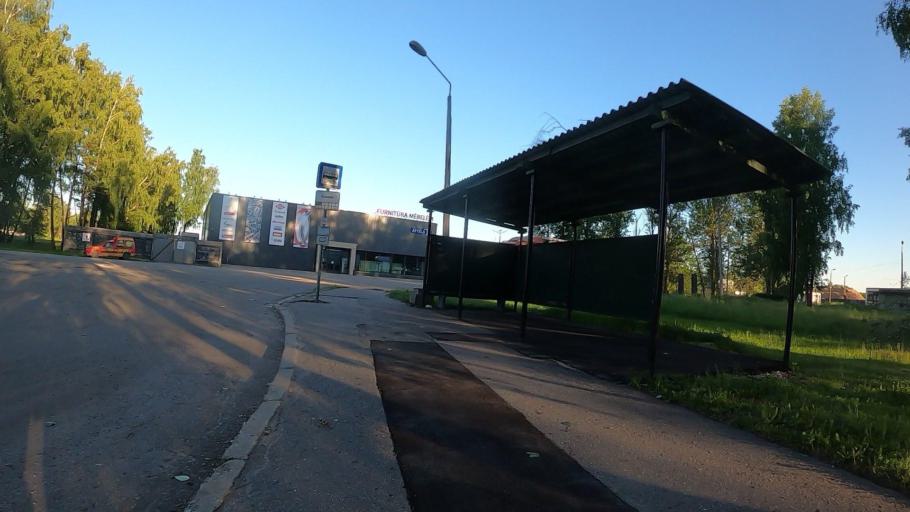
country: LV
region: Kekava
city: Kekava
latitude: 56.8818
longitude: 24.2449
